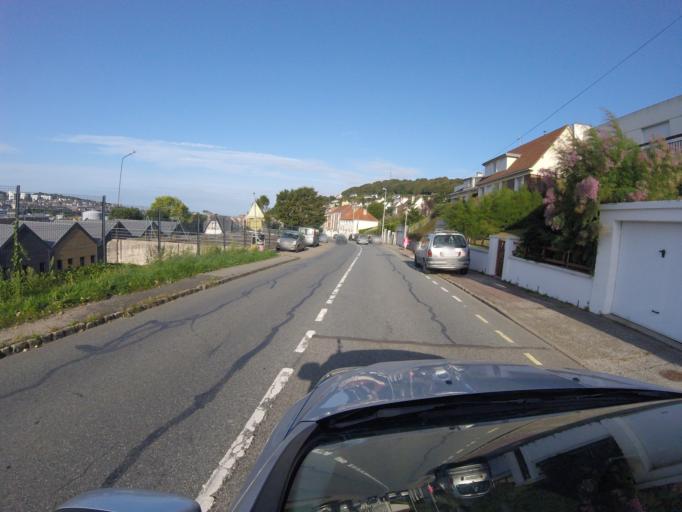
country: FR
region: Haute-Normandie
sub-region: Departement de la Seine-Maritime
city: Fecamp
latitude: 49.7619
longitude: 0.3828
